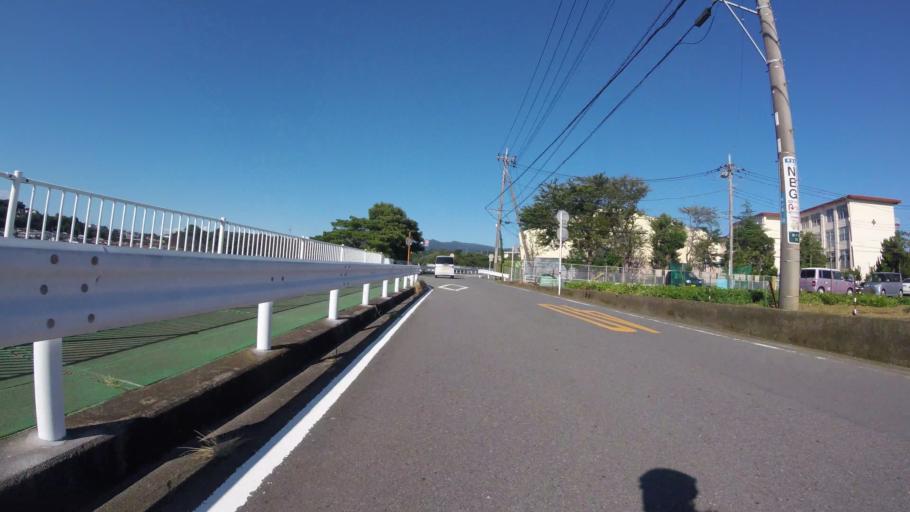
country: JP
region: Shizuoka
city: Mishima
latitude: 35.1329
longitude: 138.9327
